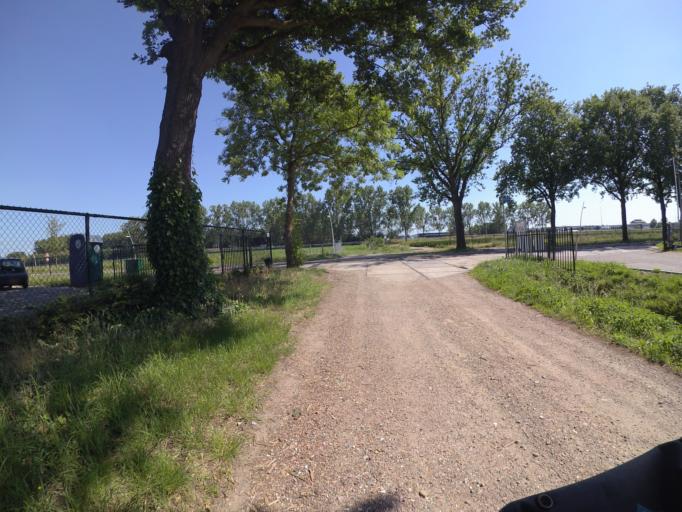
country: NL
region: North Brabant
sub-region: Gemeente Heusden
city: Heusden
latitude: 51.6998
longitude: 5.1575
